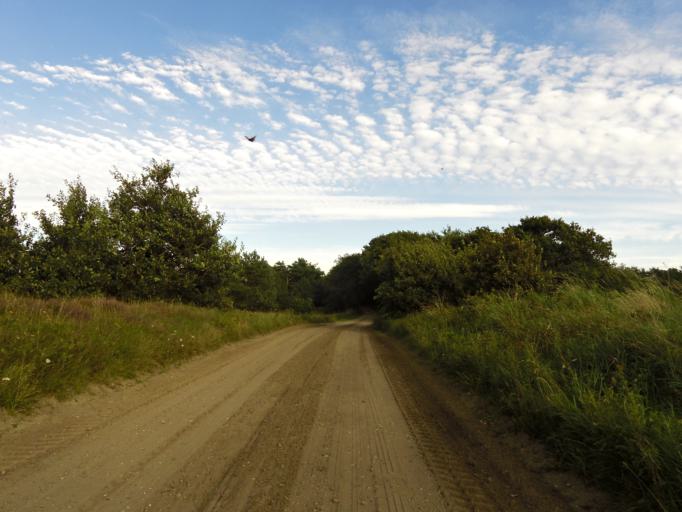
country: DK
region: South Denmark
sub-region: Haderslev Kommune
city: Gram
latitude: 55.3107
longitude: 8.9185
